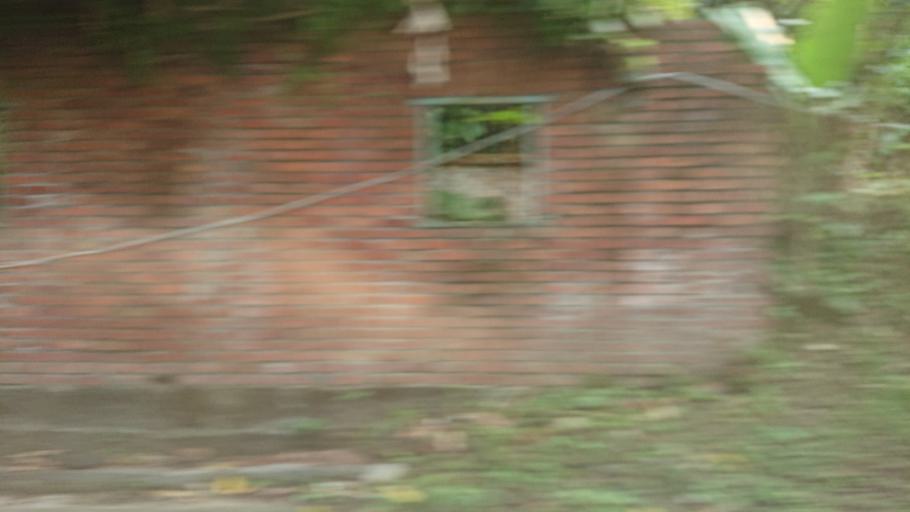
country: TW
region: Taiwan
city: Daxi
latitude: 24.8727
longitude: 121.3875
